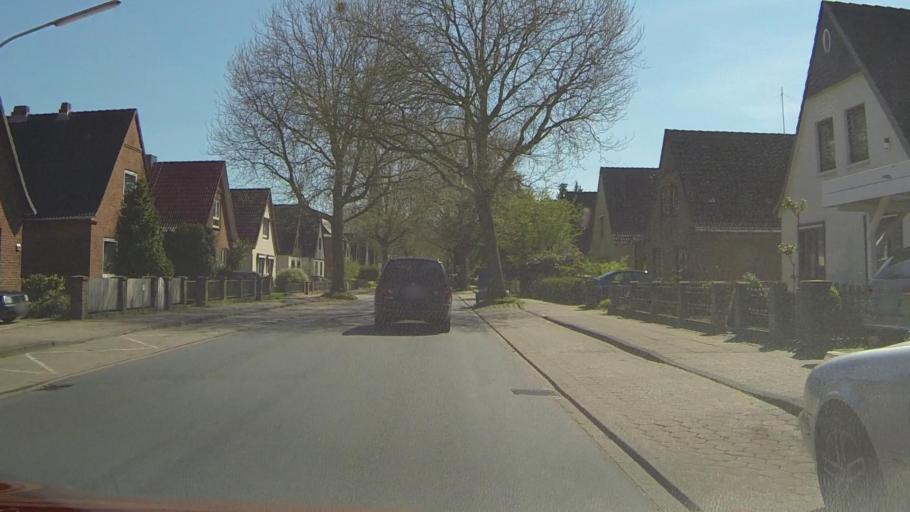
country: DE
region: Schleswig-Holstein
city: Uetersen
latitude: 53.6893
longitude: 9.6850
